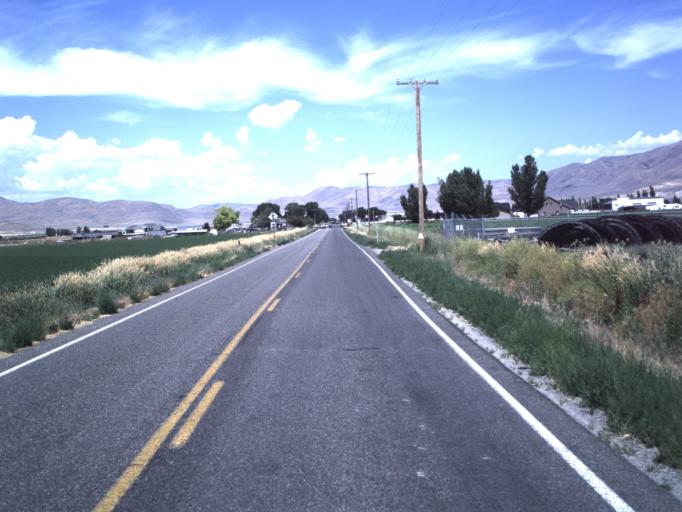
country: US
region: Utah
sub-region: Box Elder County
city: Tremonton
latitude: 41.6958
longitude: -112.2778
